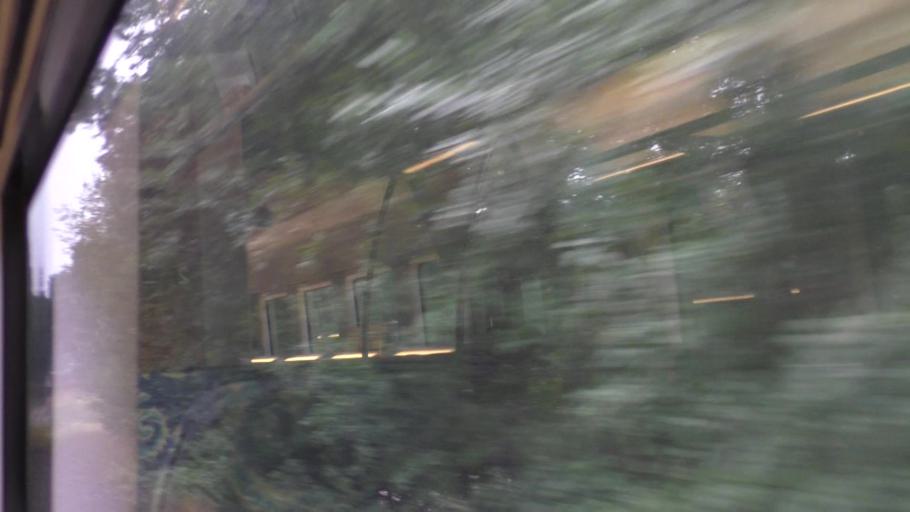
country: DE
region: Saxony
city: Goerlitz
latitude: 51.1751
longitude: 14.9666
